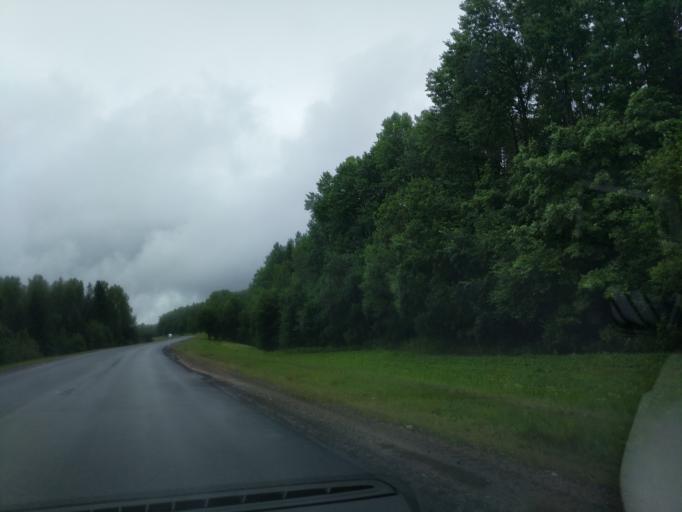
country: BY
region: Minsk
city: Syomkava
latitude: 54.2494
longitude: 27.4871
